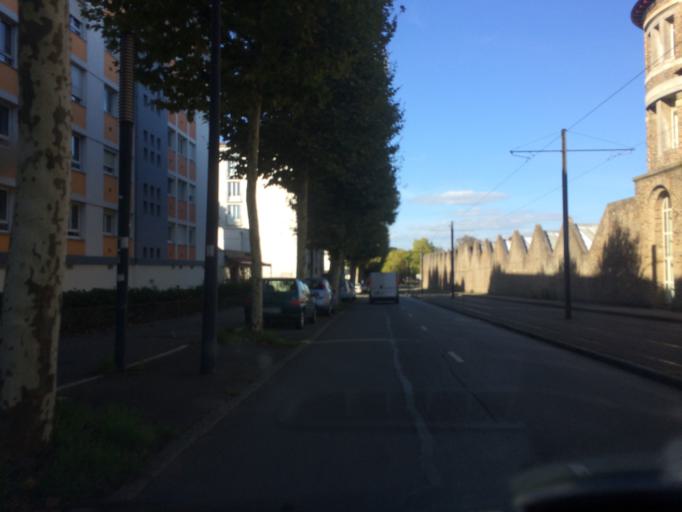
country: FR
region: Pays de la Loire
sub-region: Departement de la Loire-Atlantique
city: Nantes
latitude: 47.2389
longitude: -1.5566
